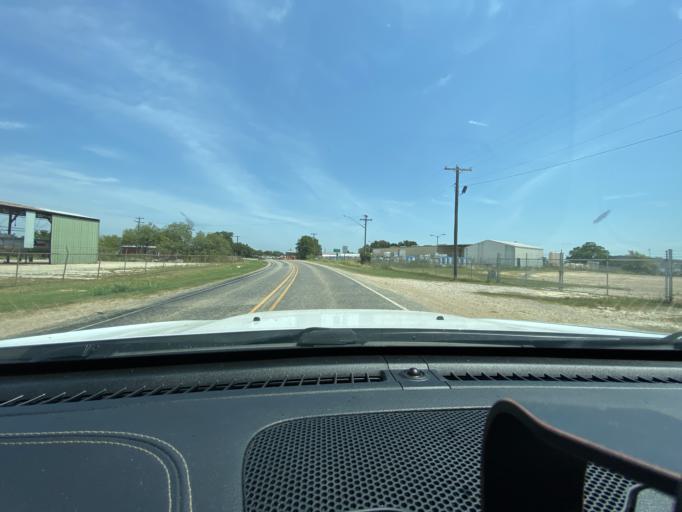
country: US
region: Texas
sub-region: Lee County
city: Giddings
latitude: 30.1675
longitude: -96.9414
